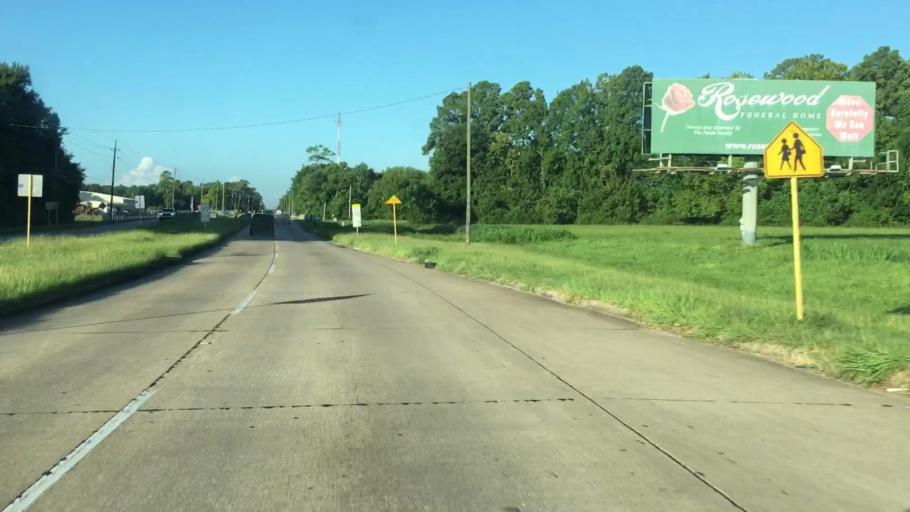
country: US
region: Texas
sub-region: Harris County
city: Humble
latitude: 29.9557
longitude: -95.2670
